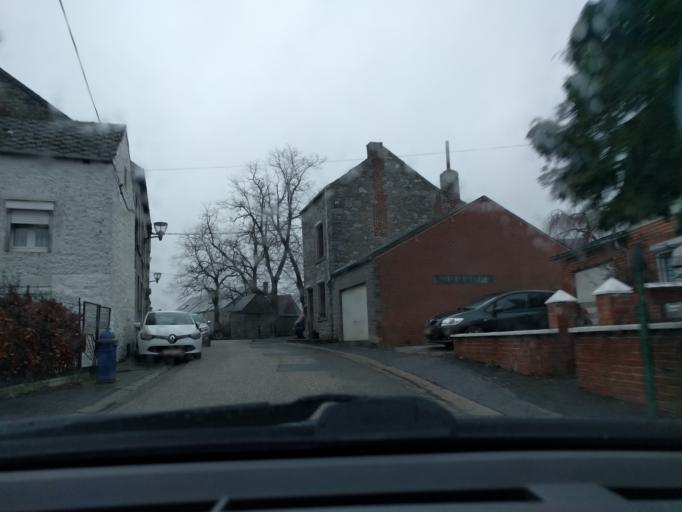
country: BE
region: Wallonia
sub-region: Province de Namur
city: Couvin
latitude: 50.0498
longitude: 4.5022
